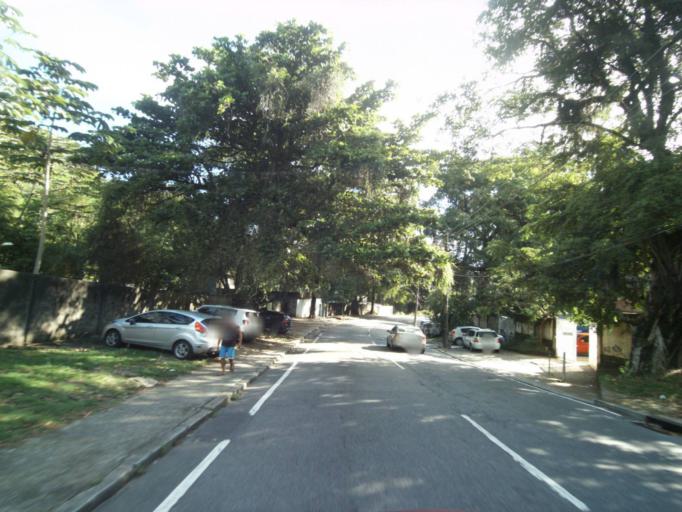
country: BR
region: Rio de Janeiro
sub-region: Rio De Janeiro
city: Rio de Janeiro
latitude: -22.9266
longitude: -43.3162
